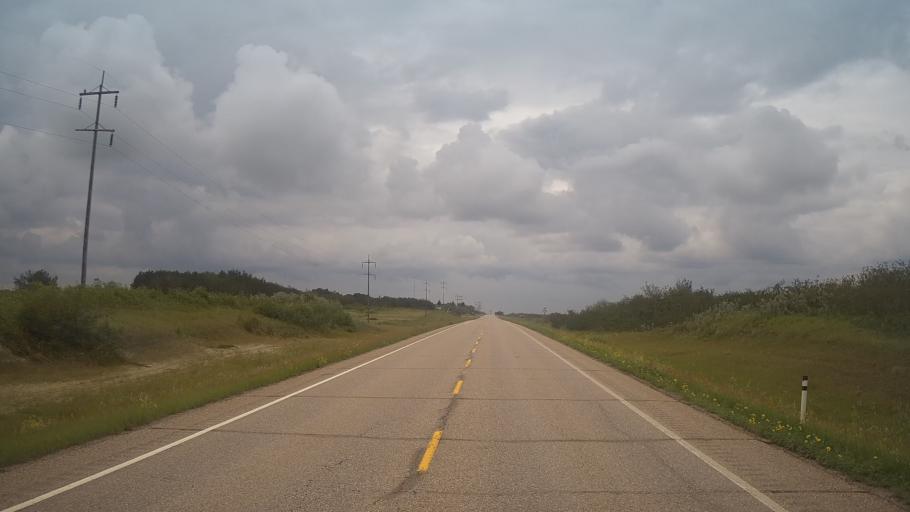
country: CA
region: Alberta
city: Wainwright
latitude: 52.5595
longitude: -111.0411
